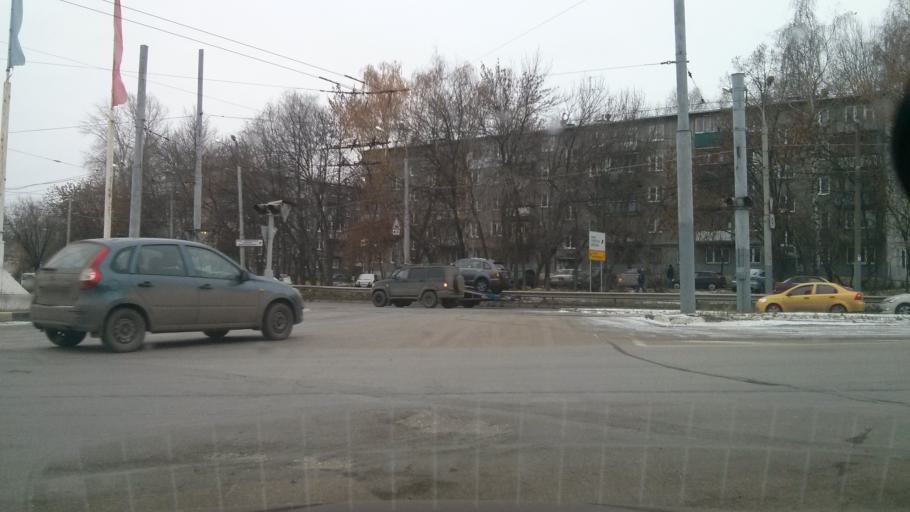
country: RU
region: Nizjnij Novgorod
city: Nizhniy Novgorod
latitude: 56.3032
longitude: 44.0450
